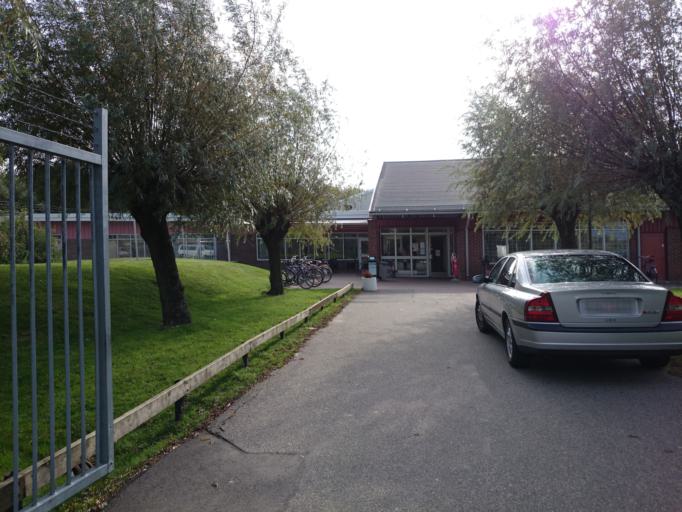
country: SE
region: Skane
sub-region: Malmo
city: Bunkeflostrand
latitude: 55.5709
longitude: 12.9711
